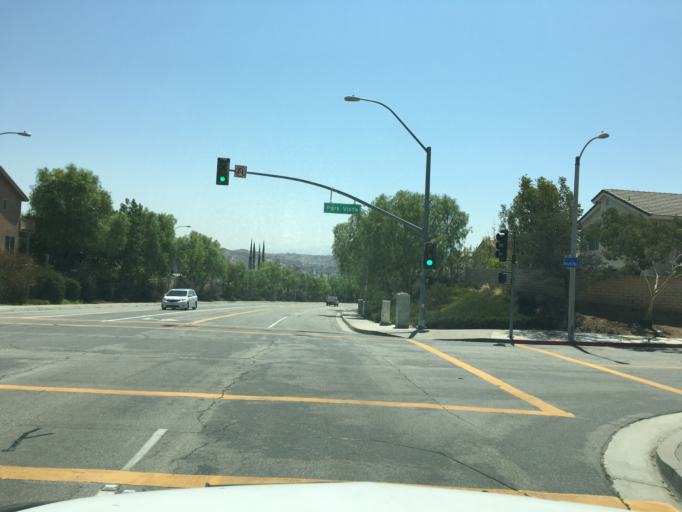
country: US
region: California
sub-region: Los Angeles County
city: Castaic
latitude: 34.4724
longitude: -118.6301
